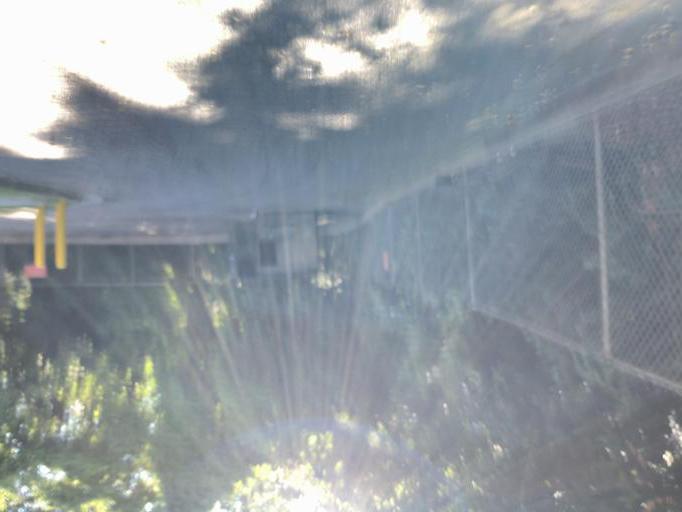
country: US
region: Georgia
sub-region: DeKalb County
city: North Decatur
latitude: 33.7896
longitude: -84.3079
